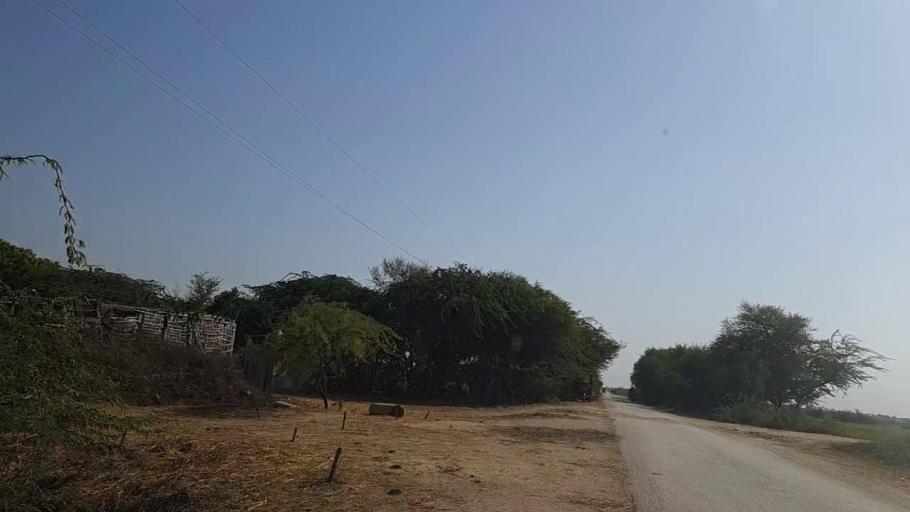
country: PK
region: Sindh
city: Mirpur Batoro
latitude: 24.6392
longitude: 68.2912
